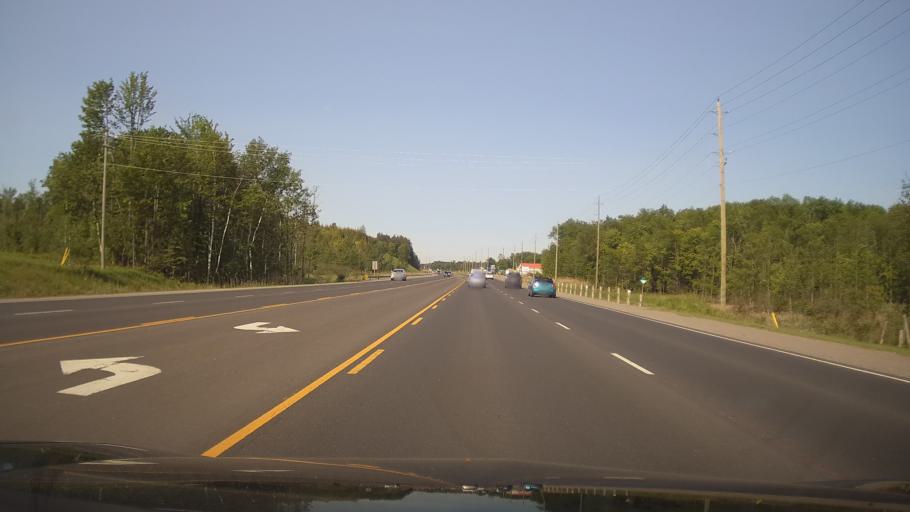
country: CA
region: Ontario
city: Peterborough
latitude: 44.3106
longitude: -78.2262
